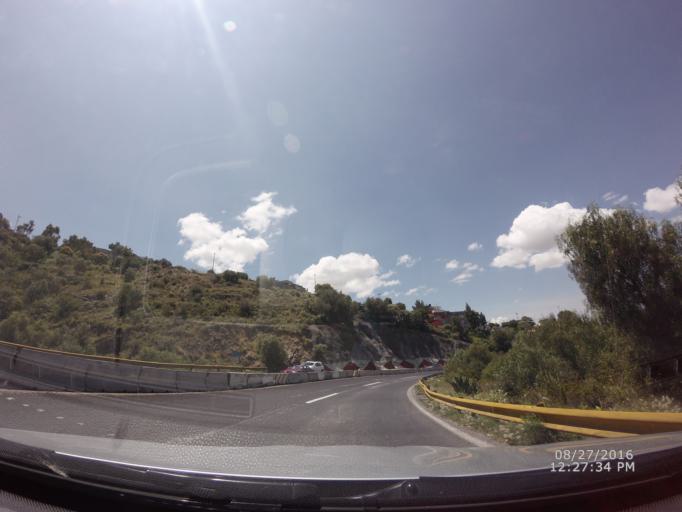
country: MX
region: Hidalgo
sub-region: Mineral de la Reforma
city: Colonia Militar
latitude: 20.1219
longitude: -98.6948
